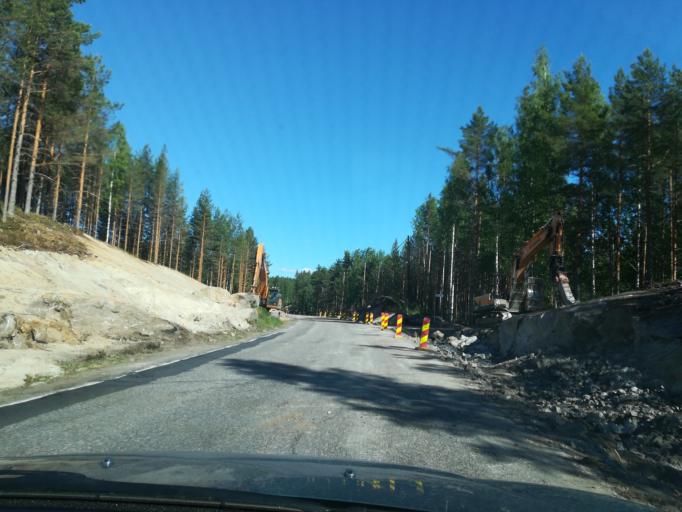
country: FI
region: Southern Savonia
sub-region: Mikkeli
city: Puumala
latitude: 61.4682
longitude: 28.3184
